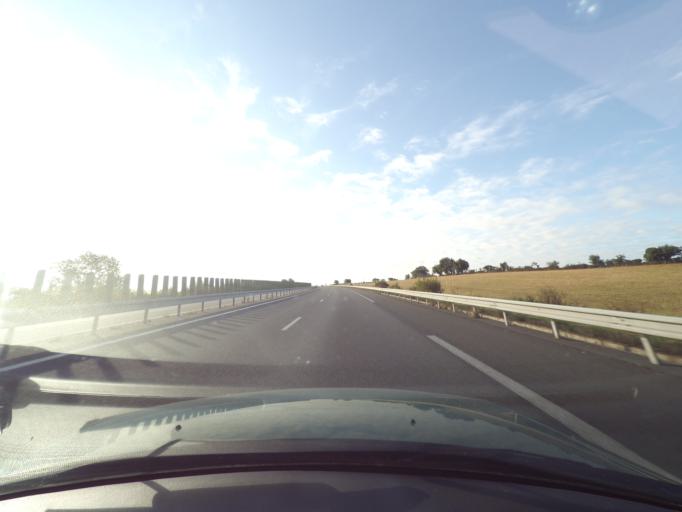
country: FR
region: Poitou-Charentes
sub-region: Departement des Deux-Sevres
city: Combrand
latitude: 46.9079
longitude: -0.6780
